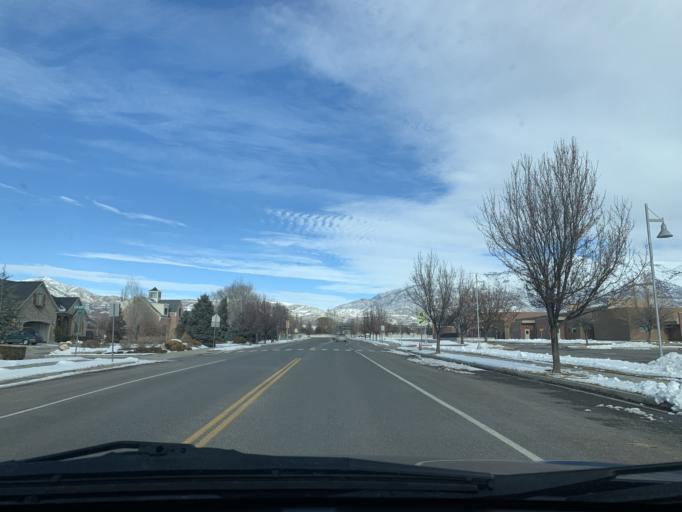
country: US
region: Utah
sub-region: Utah County
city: Lehi
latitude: 40.4185
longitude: -111.8211
